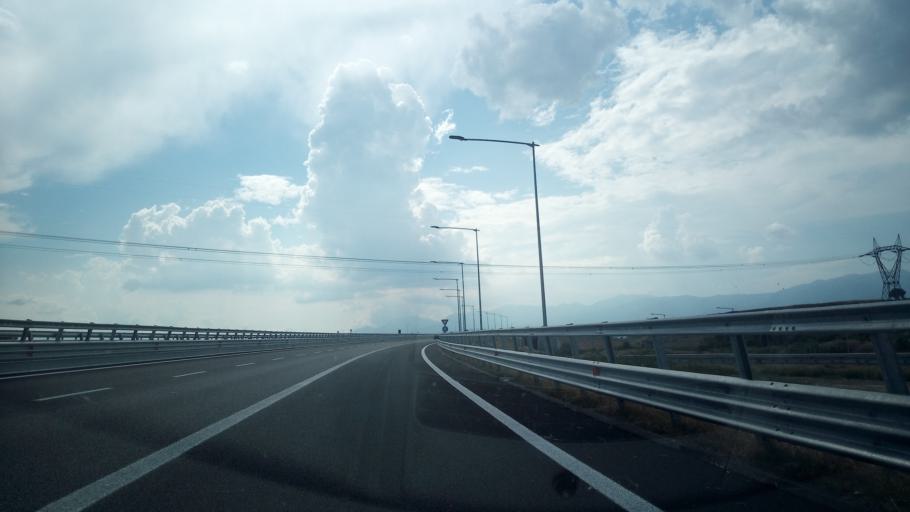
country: IT
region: Calabria
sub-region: Provincia di Cosenza
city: Doria
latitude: 39.7238
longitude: 16.3171
